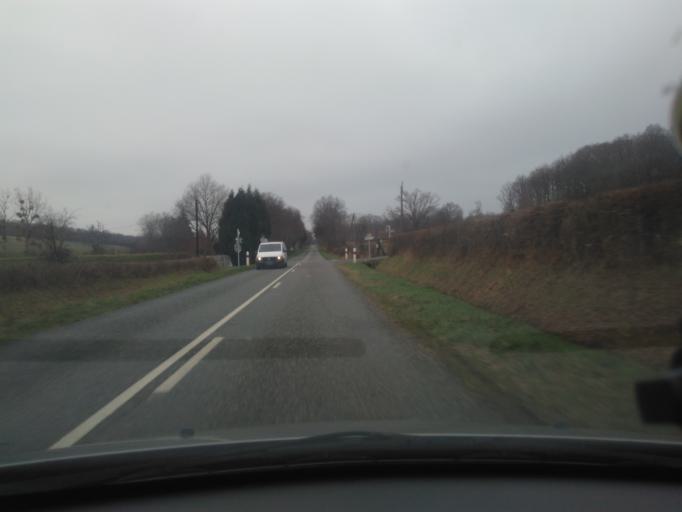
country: FR
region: Centre
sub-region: Departement du Cher
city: Chateaumeillant
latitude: 46.6339
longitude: 2.1817
